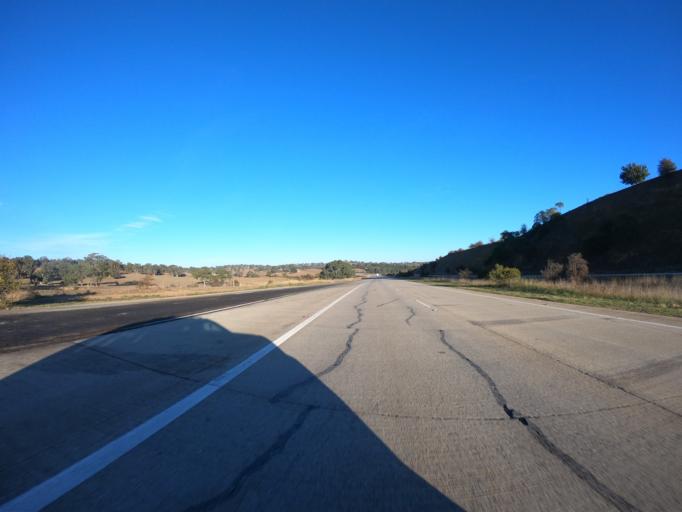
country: AU
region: New South Wales
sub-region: Yass Valley
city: Gundaroo
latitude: -35.1765
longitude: 149.2847
